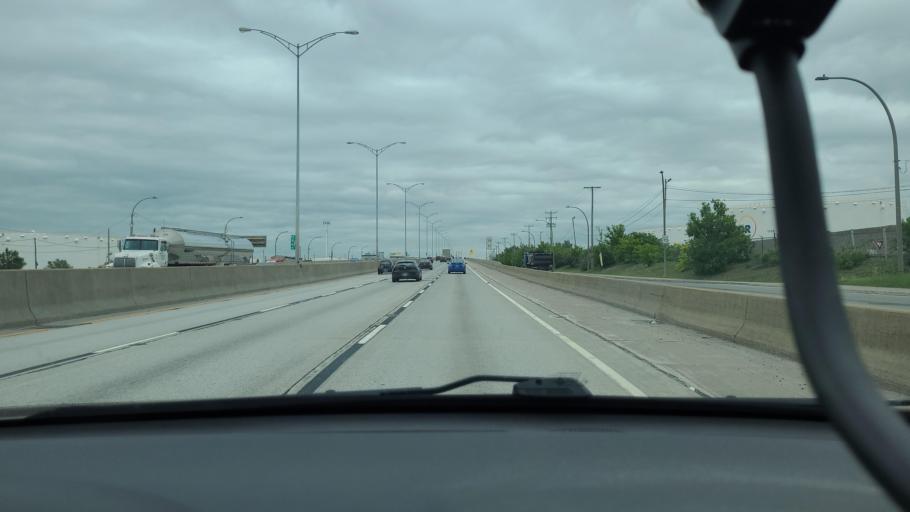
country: CA
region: Quebec
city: Montreal-Est
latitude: 45.6480
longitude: -73.5285
